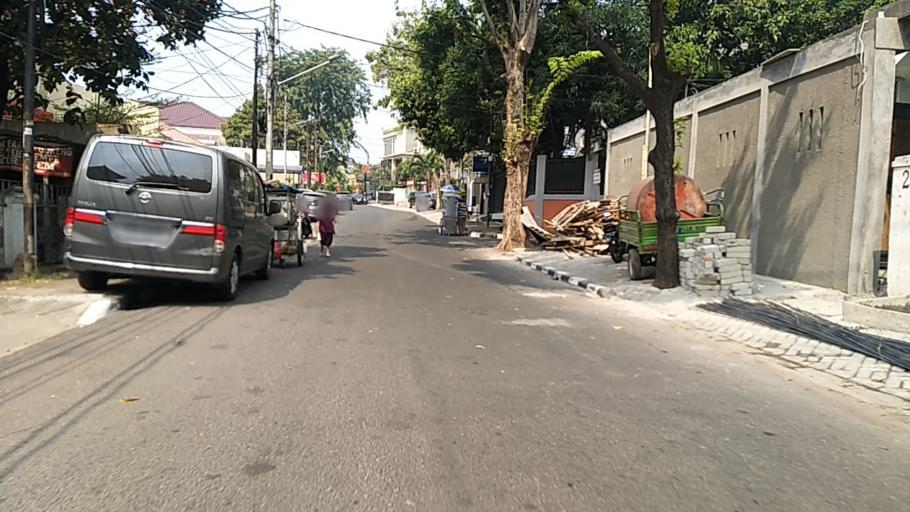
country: ID
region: Jakarta Raya
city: Jakarta
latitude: -6.2342
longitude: 106.8486
